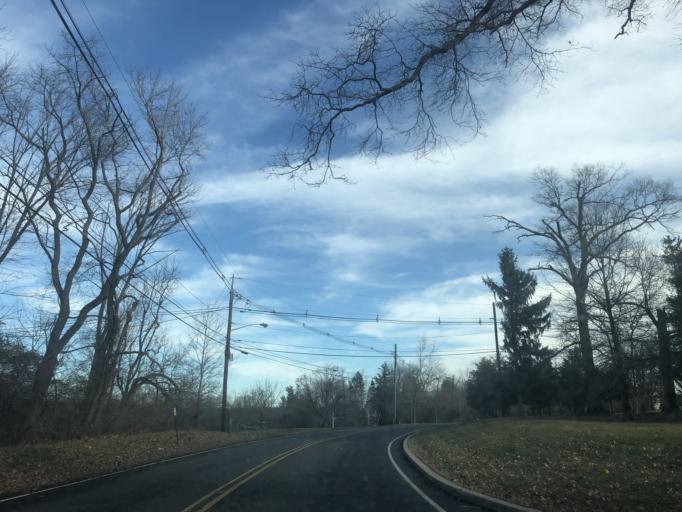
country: US
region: New Jersey
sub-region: Somerset County
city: Kingston
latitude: 40.3596
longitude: -74.6231
